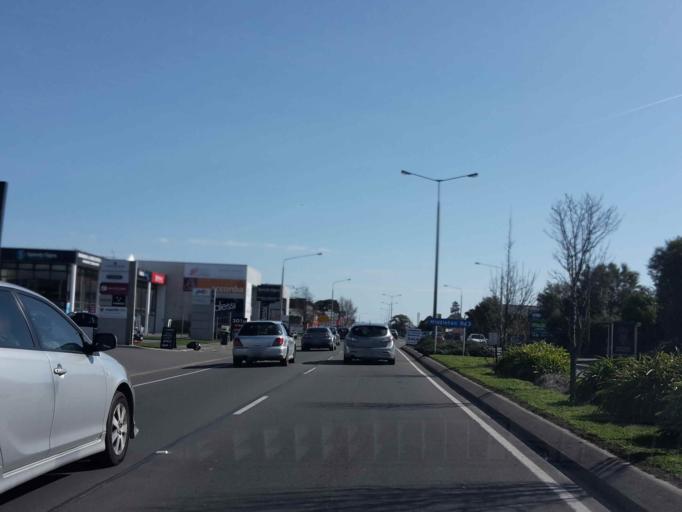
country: NZ
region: Canterbury
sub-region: Christchurch City
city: Christchurch
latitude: -43.5386
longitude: 172.5834
